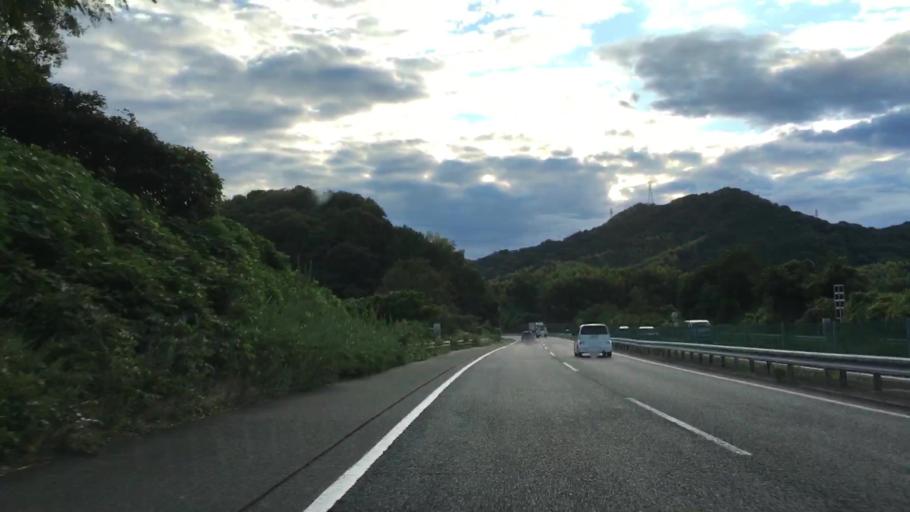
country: JP
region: Yamaguchi
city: Shimonoseki
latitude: 34.0451
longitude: 130.9940
